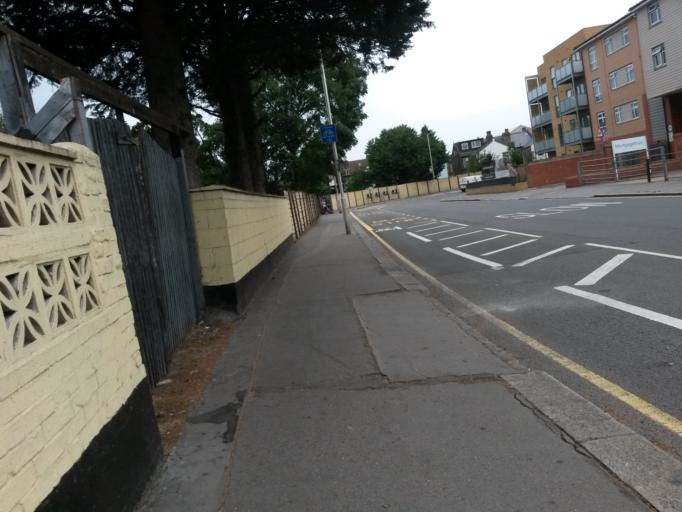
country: GB
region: England
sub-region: Greater London
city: Croydon
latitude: 51.3832
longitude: -0.0999
